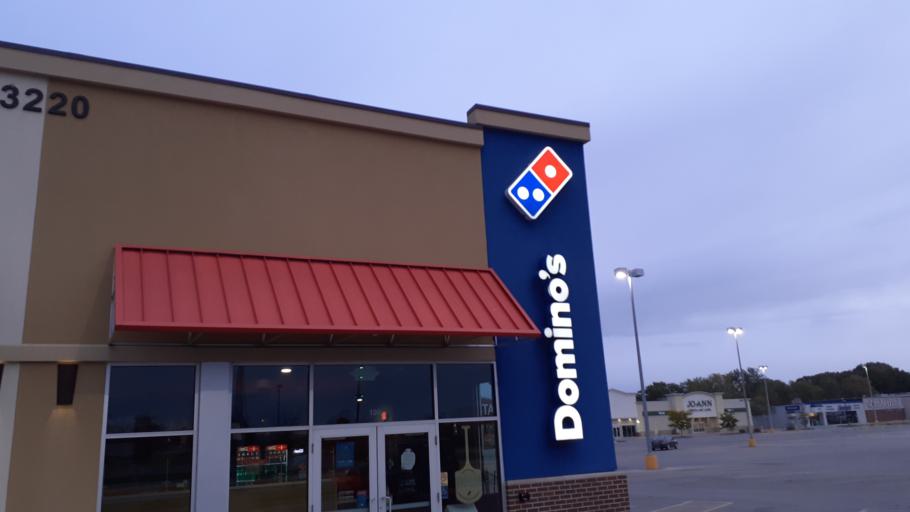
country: US
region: Iowa
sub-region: Des Moines County
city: West Burlington
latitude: 40.8150
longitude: -91.1402
